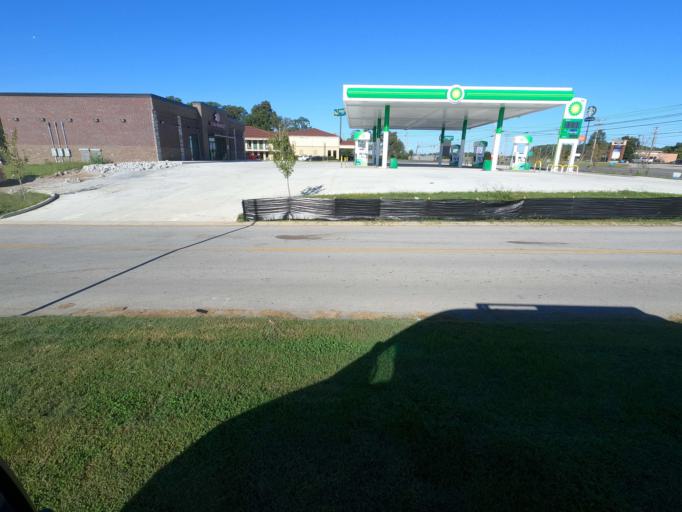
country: US
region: Tennessee
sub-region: Coffee County
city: Manchester
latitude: 35.4558
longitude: -86.0484
